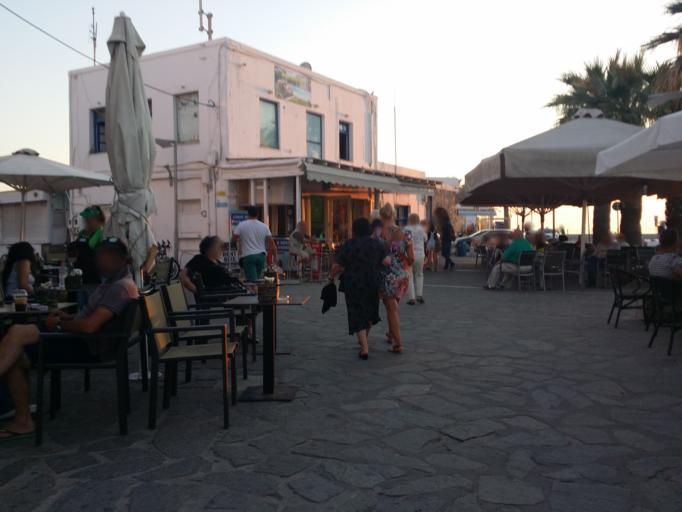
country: GR
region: South Aegean
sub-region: Nomos Kykladon
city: Paros
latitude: 37.0861
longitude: 25.1500
